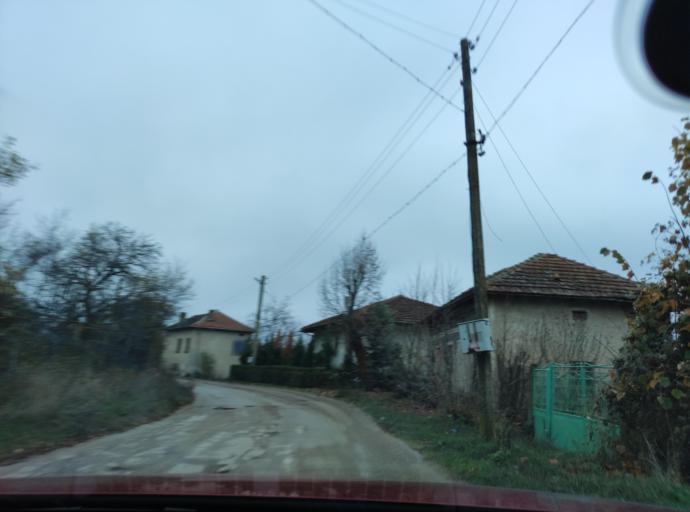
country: BG
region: Lovech
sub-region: Obshtina Yablanitsa
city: Yablanitsa
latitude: 43.0944
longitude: 24.0755
